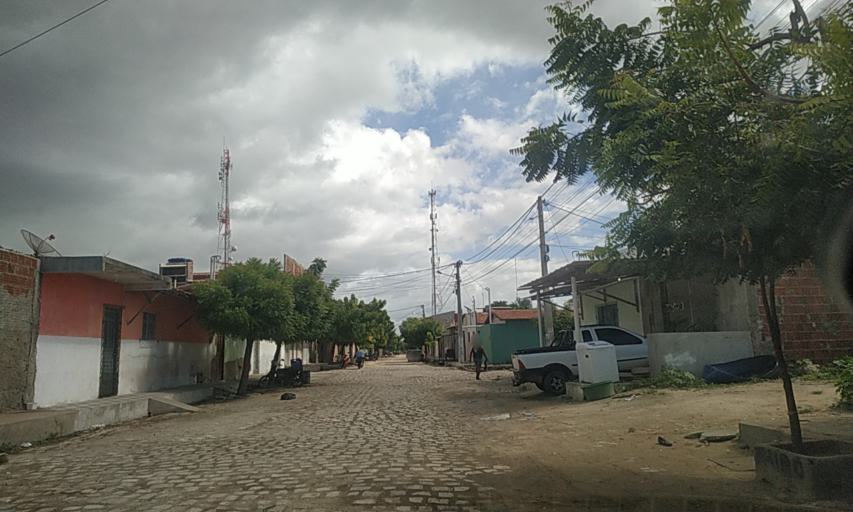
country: BR
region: Rio Grande do Norte
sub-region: Areia Branca
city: Areia Branca
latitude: -4.9511
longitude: -37.1254
